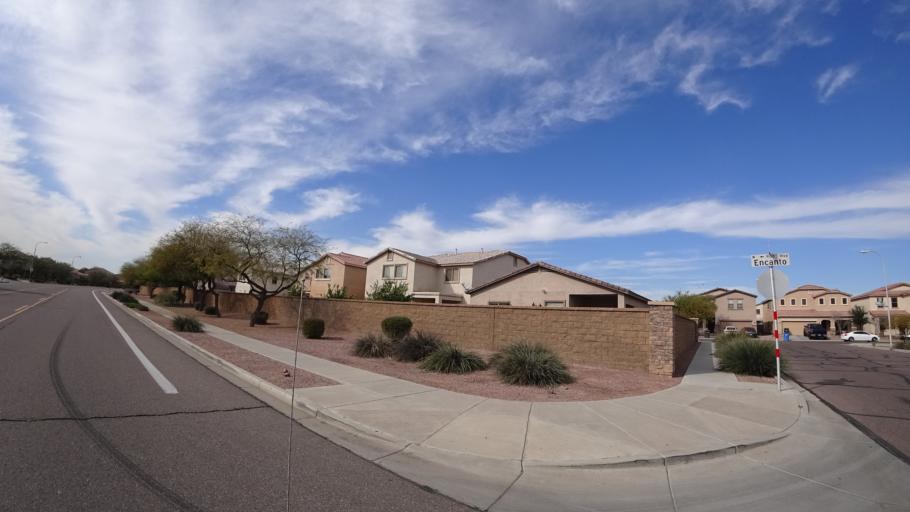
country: US
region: Arizona
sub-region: Maricopa County
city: Tolleson
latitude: 33.4723
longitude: -112.2565
